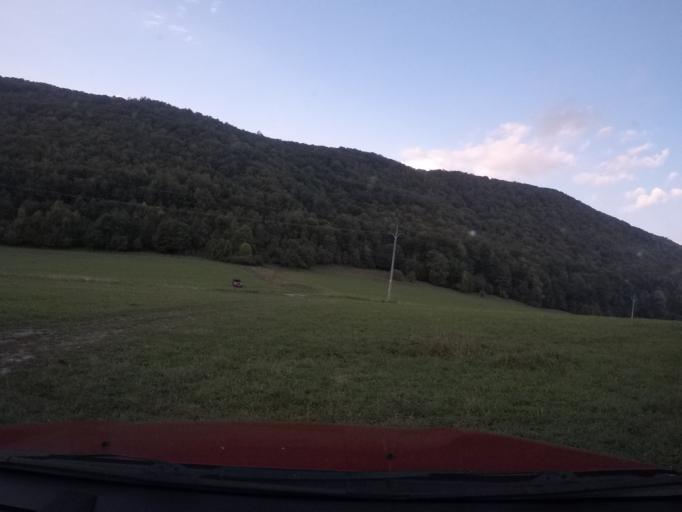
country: SK
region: Kosicky
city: Medzev
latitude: 48.6334
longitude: 20.7840
